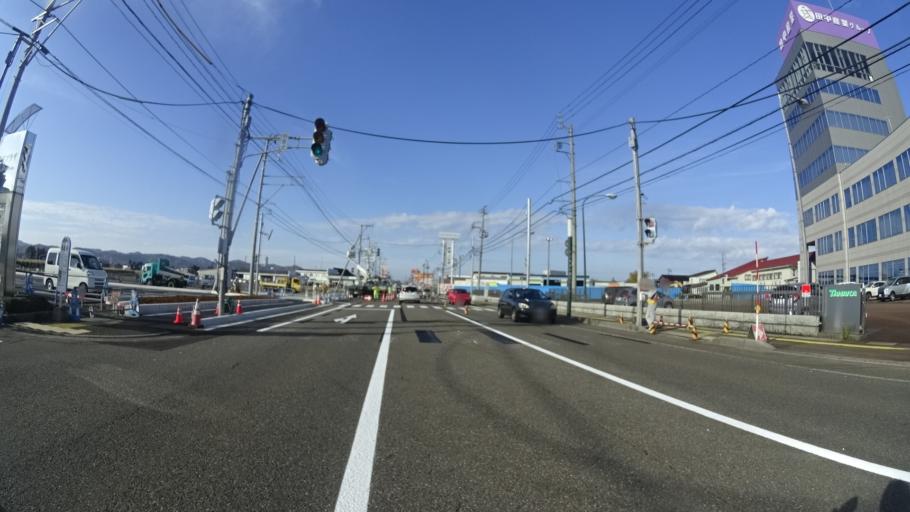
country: JP
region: Niigata
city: Joetsu
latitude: 37.1308
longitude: 138.2454
